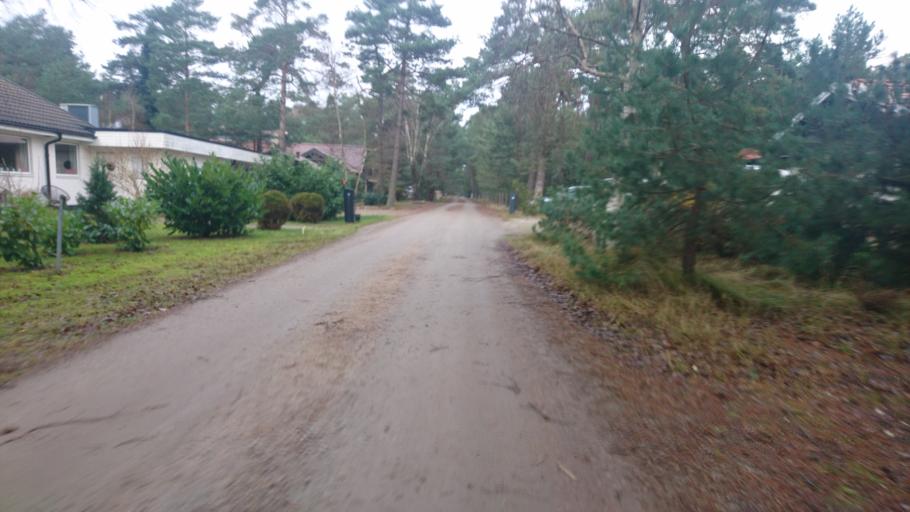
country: SE
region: Skane
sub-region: Vellinge Kommun
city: Ljunghusen
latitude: 55.3912
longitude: 12.9157
